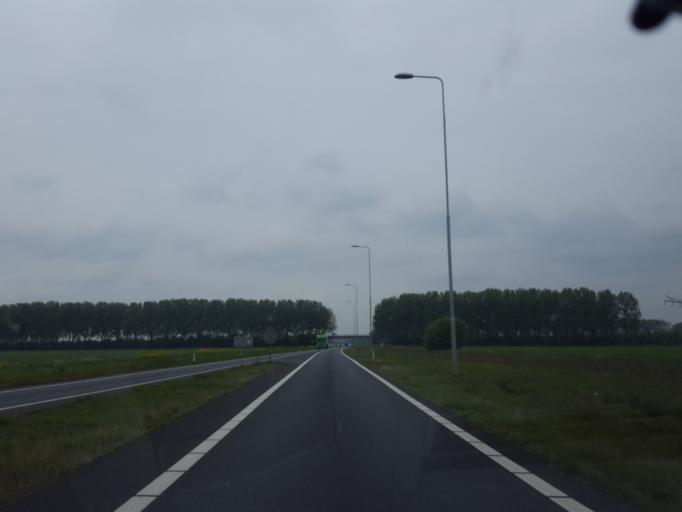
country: NL
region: Gelderland
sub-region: Gemeente Wijchen
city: Bergharen
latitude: 51.8634
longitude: 5.6963
